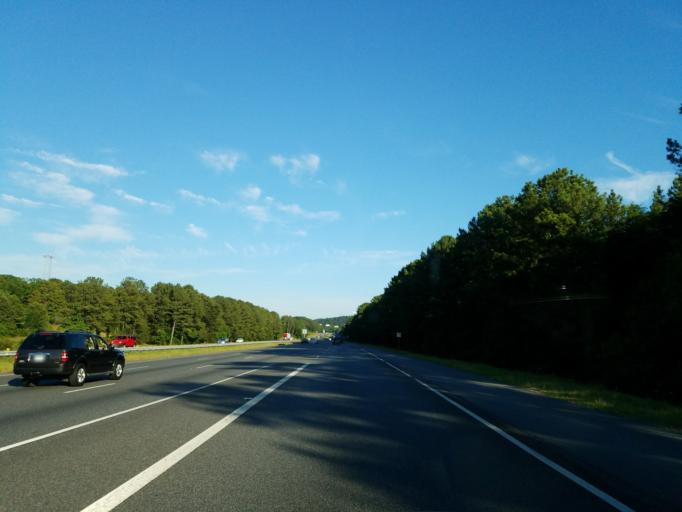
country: US
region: Georgia
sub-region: Bartow County
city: Adairsville
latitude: 34.3736
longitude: -84.9083
